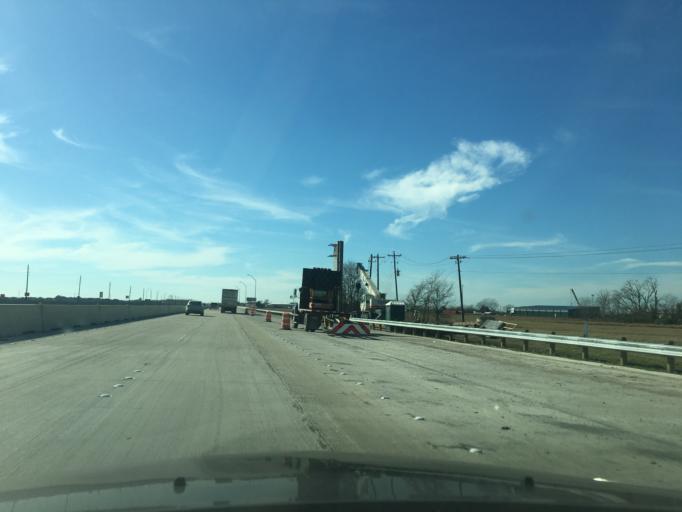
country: US
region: Texas
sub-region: Fort Bend County
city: Pleak
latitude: 29.4911
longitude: -95.9195
